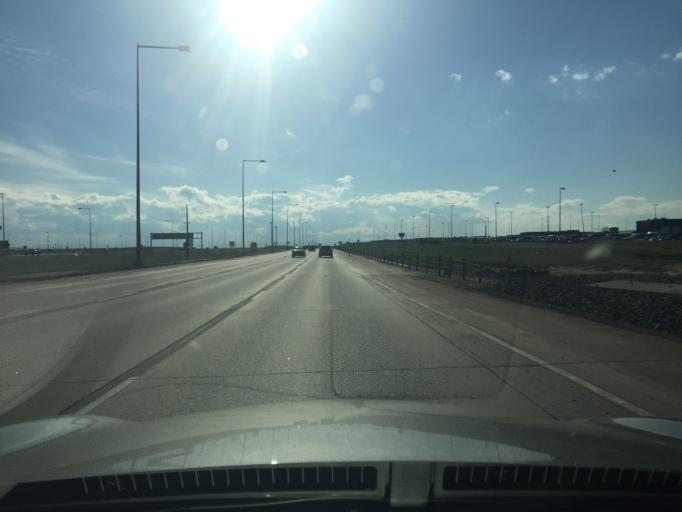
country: US
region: Colorado
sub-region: Adams County
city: Aurora
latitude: 39.8344
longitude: -104.7010
